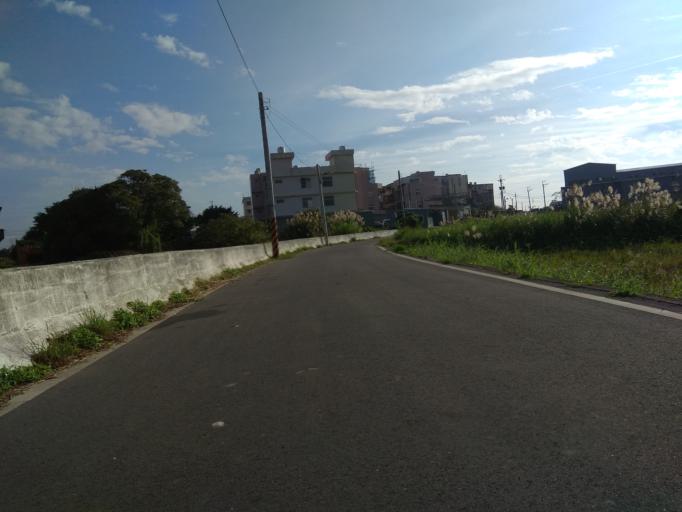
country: TW
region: Taiwan
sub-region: Hsinchu
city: Zhubei
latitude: 24.9824
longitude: 121.0524
